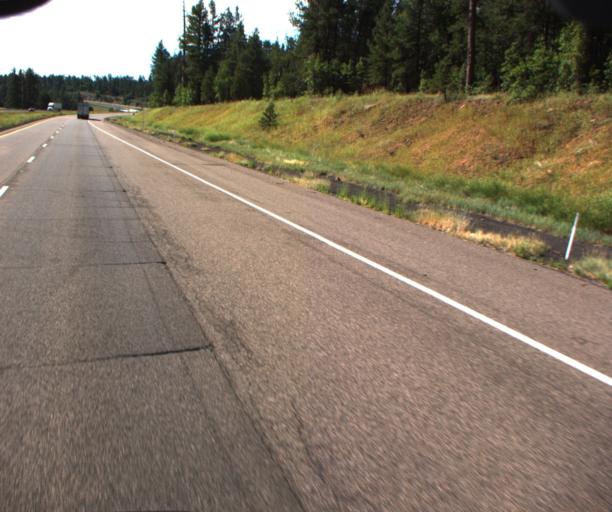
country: US
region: Arizona
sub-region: Coconino County
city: Sedona
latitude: 34.8709
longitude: -111.6315
